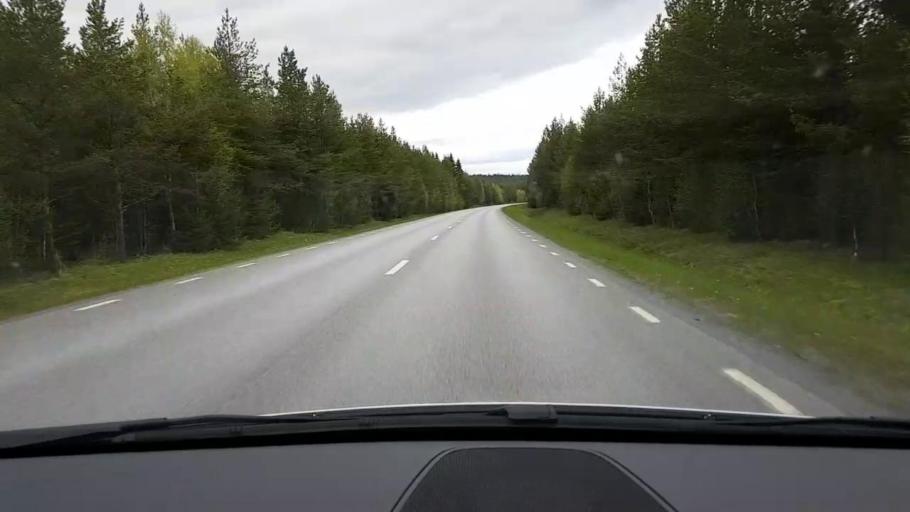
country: SE
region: Jaemtland
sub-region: Krokoms Kommun
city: Valla
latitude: 63.2861
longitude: 13.9290
